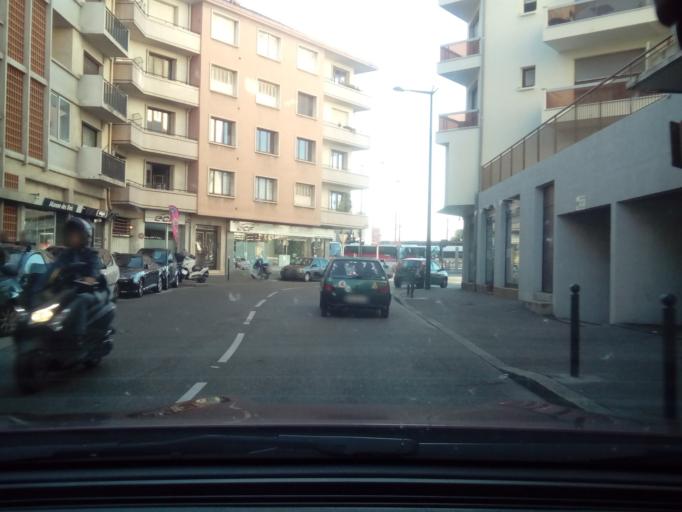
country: FR
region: Rhone-Alpes
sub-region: Departement de la Haute-Savoie
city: Annecy
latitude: 45.9009
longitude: 6.1201
